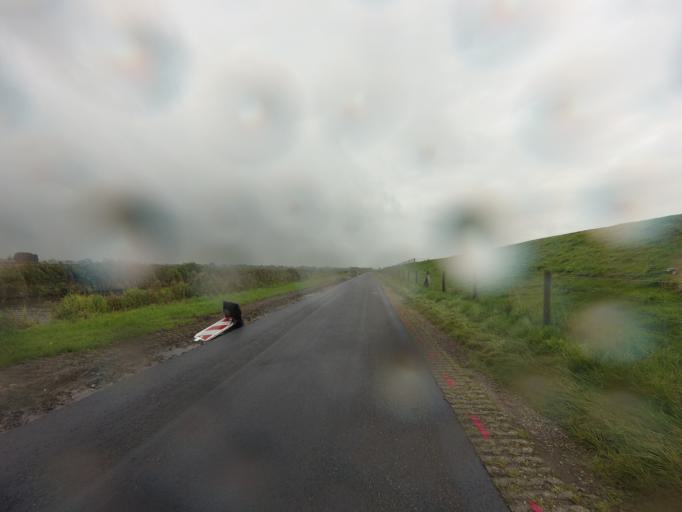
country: NL
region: Friesland
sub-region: Sudwest Fryslan
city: Koudum
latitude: 52.9183
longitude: 5.4109
